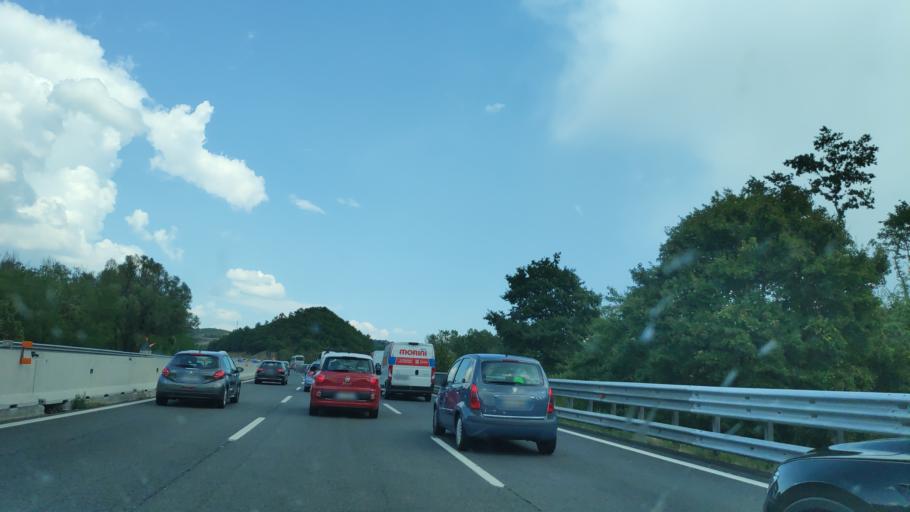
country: IT
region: Umbria
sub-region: Provincia di Terni
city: Ficulle
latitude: 42.8223
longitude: 12.0385
